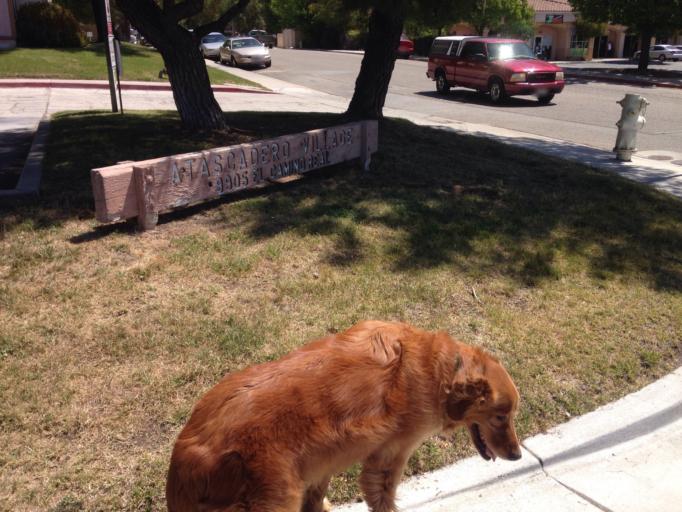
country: US
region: California
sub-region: San Luis Obispo County
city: Atascadero
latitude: 35.4642
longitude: -120.6469
